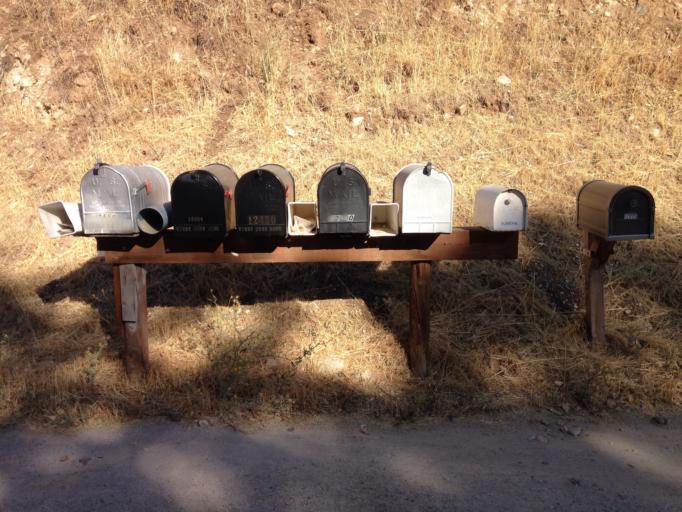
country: US
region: California
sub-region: San Luis Obispo County
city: Atascadero
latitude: 35.4493
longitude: -120.6275
